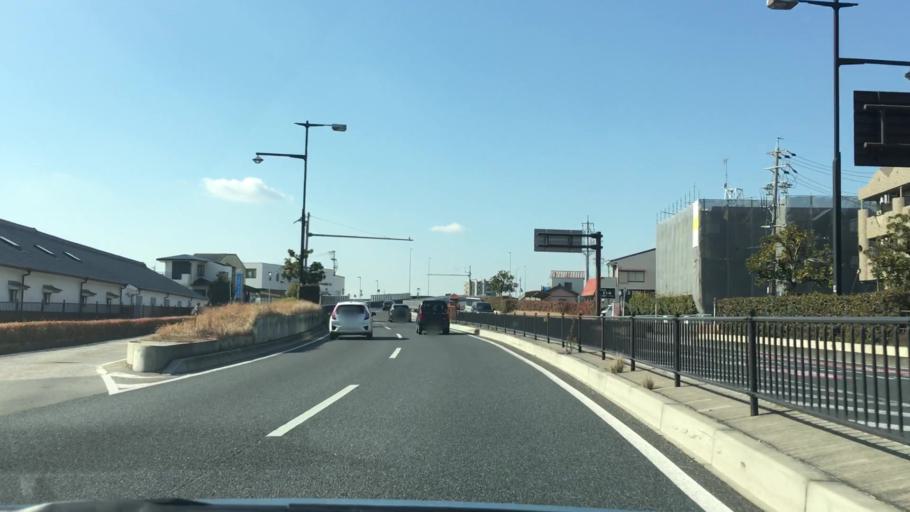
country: JP
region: Aichi
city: Okazaki
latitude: 34.9588
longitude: 137.1534
